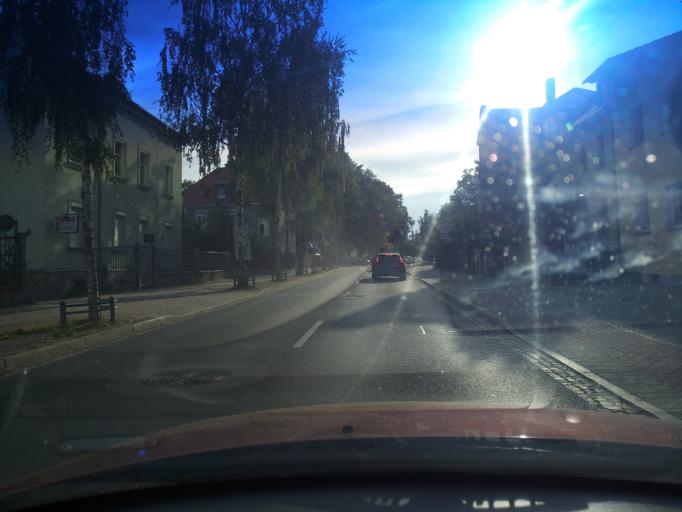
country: DE
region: Saxony
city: Bautzen
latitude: 51.1843
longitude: 14.4359
